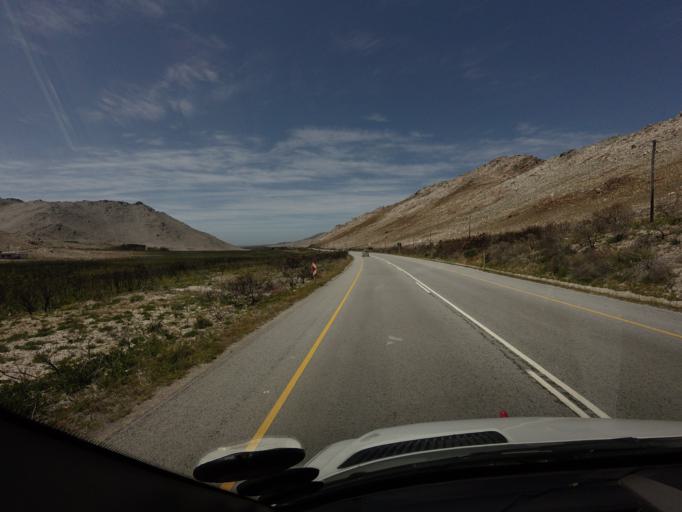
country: ZA
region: Western Cape
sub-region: Overberg District Municipality
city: Grabouw
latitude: -34.3091
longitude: 18.8279
